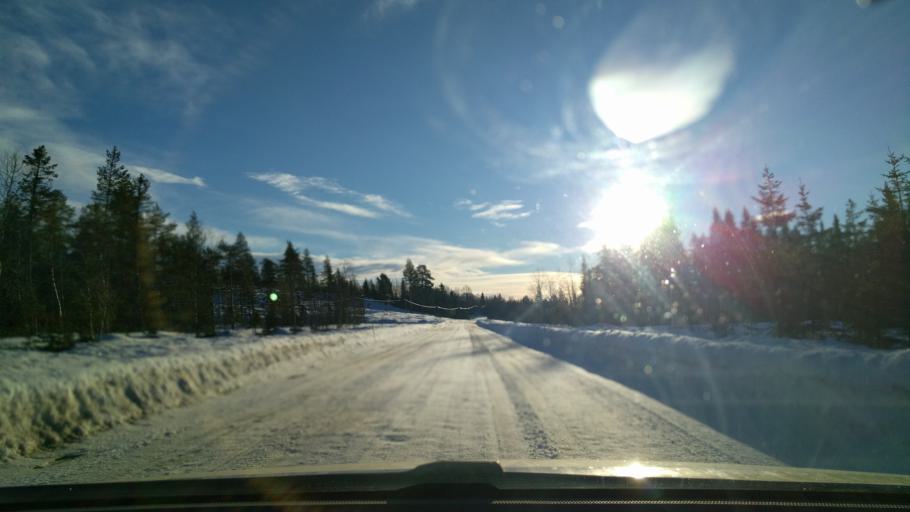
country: NO
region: Hedmark
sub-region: Trysil
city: Innbygda
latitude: 61.0835
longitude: 12.2085
